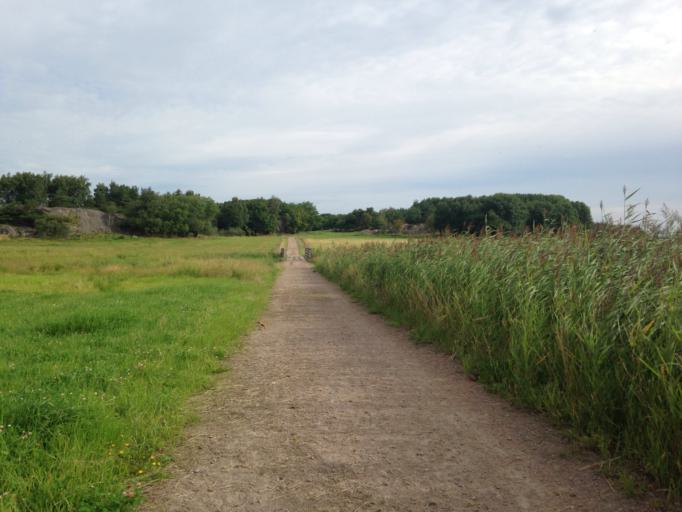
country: SE
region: Vaestra Goetaland
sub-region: Kungalvs Kommun
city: Kungalv
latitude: 57.8080
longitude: 11.8854
